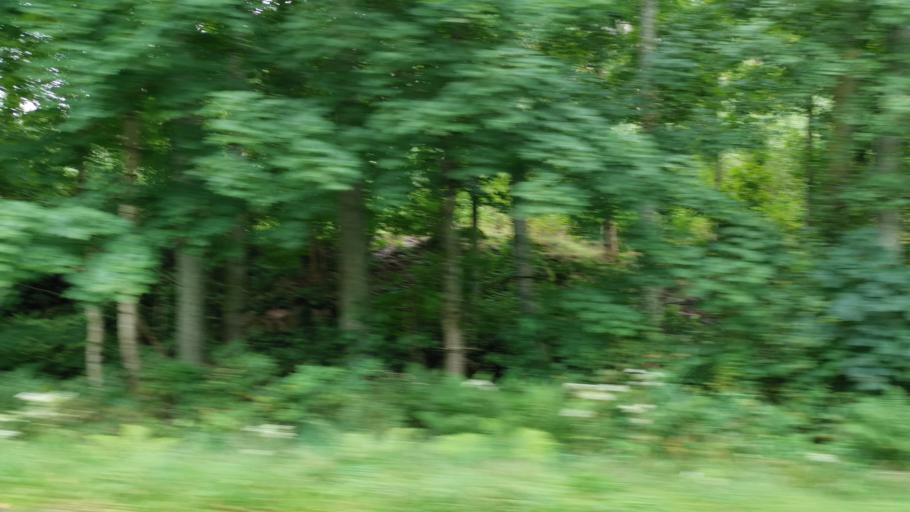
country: SE
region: Vaestra Goetaland
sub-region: Sotenas Kommun
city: Hunnebostrand
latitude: 58.4865
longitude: 11.3741
